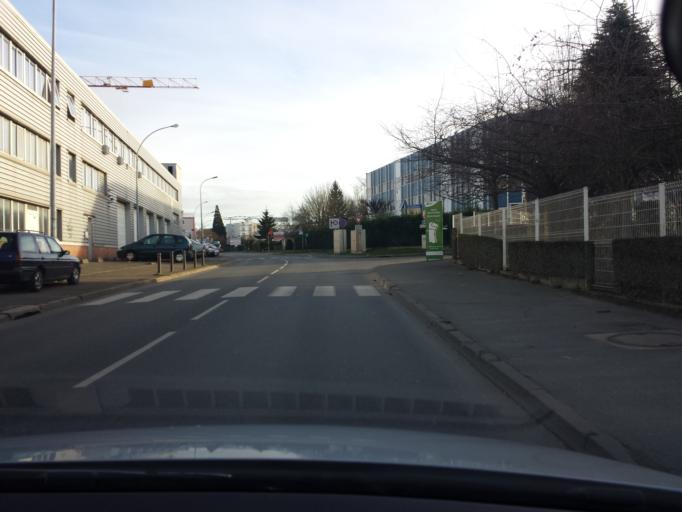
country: FR
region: Ile-de-France
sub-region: Departement de l'Essonne
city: Palaiseau
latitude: 48.7211
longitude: 2.2612
